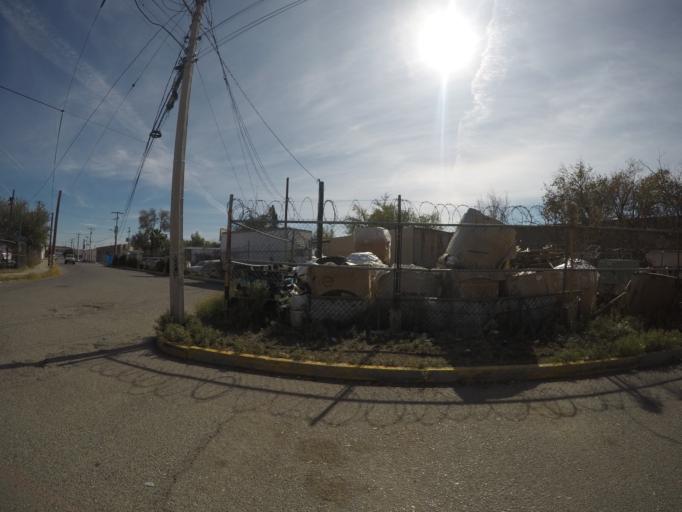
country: MX
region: Chihuahua
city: Ciudad Juarez
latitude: 31.7352
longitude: -106.4518
